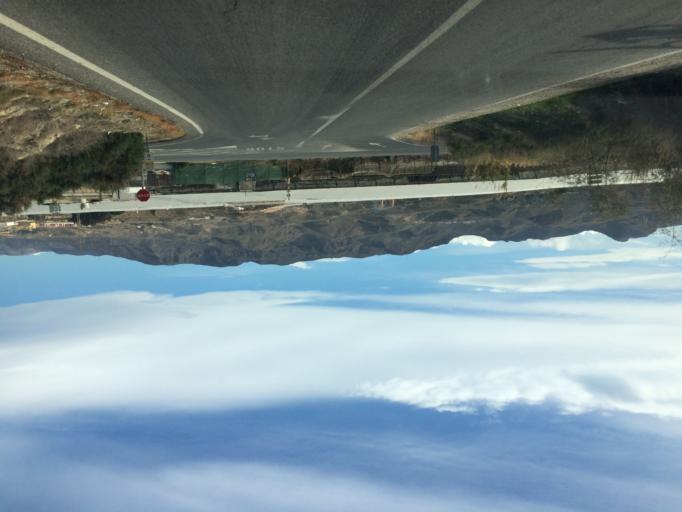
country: ES
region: Andalusia
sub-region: Provincia de Almeria
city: Pechina
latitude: 36.9227
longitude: -2.4454
